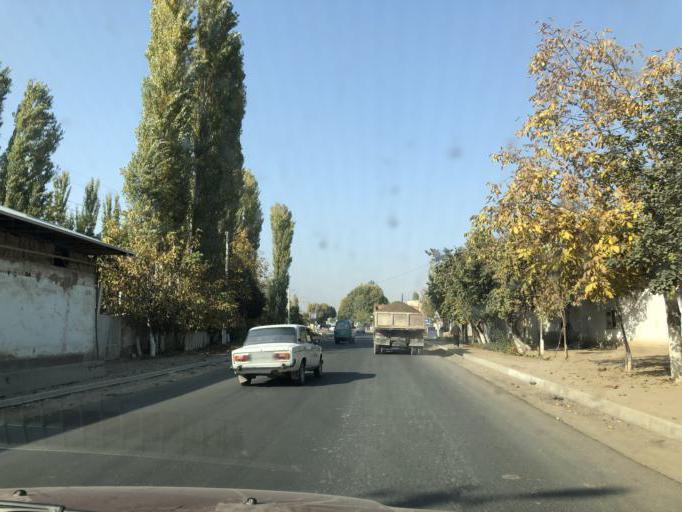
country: UZ
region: Namangan
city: Chust Shahri
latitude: 41.0706
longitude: 71.2046
